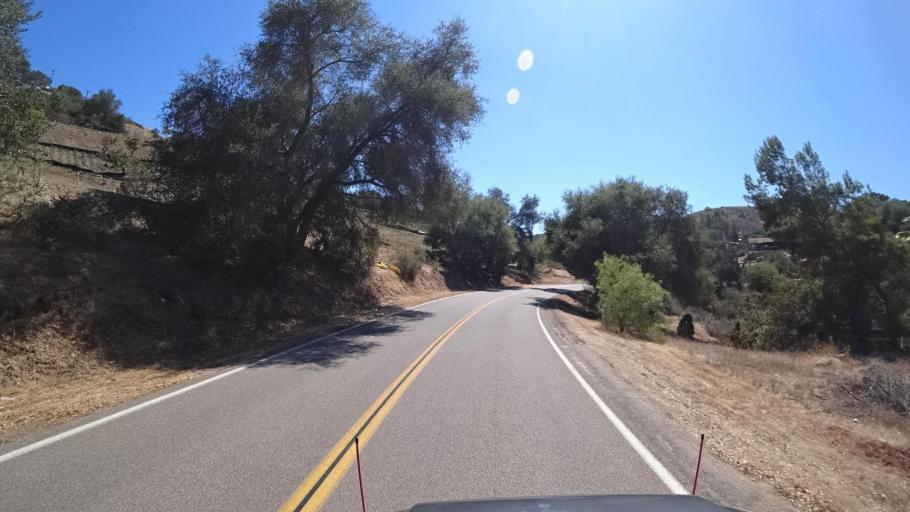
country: US
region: California
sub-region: San Diego County
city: Hidden Meadows
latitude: 33.2697
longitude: -117.0905
